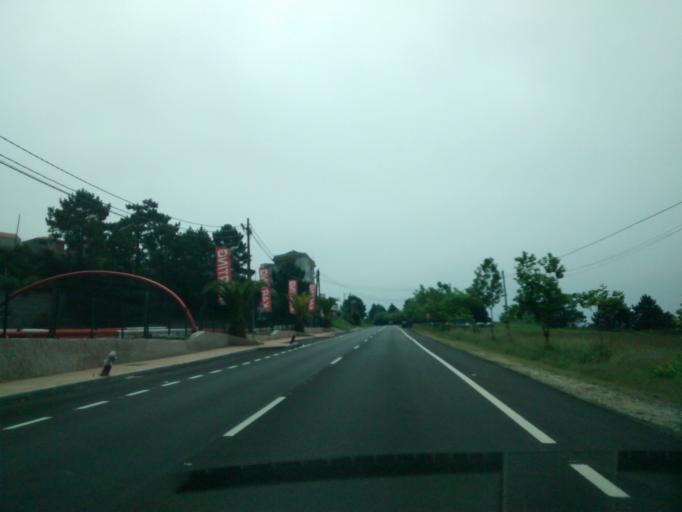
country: ES
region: Galicia
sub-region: Provincia de Pontevedra
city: Sanxenxo
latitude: 42.4147
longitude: -8.8664
